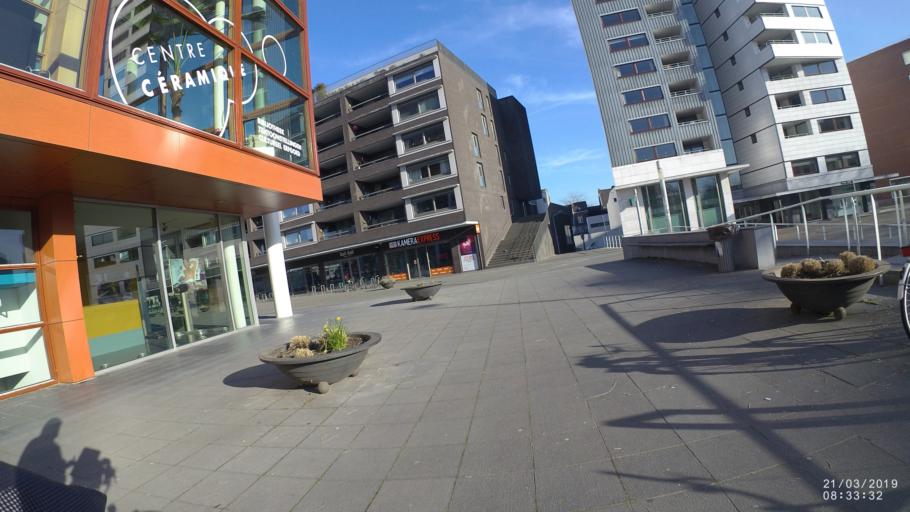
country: NL
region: Limburg
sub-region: Gemeente Maastricht
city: Maastricht
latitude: 50.8462
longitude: 5.7014
